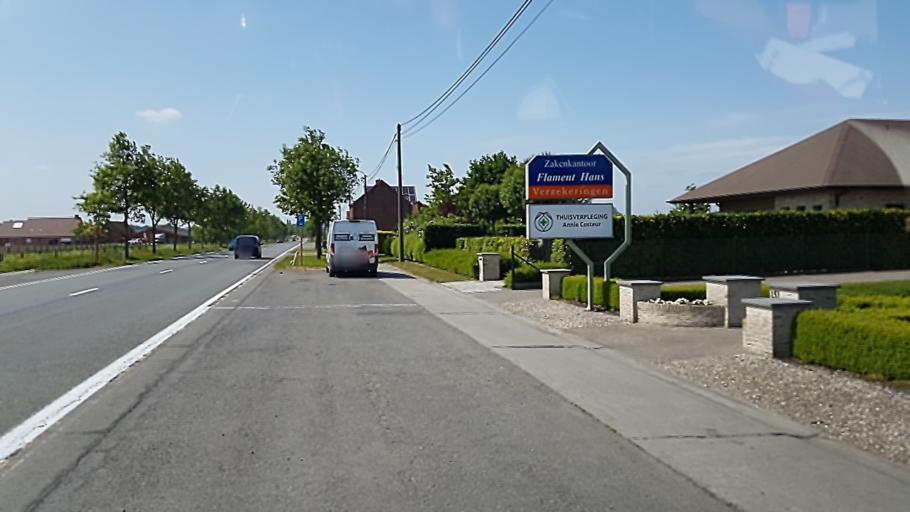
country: BE
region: Flanders
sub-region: Provincie West-Vlaanderen
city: Wervik
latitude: 50.8144
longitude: 3.0606
